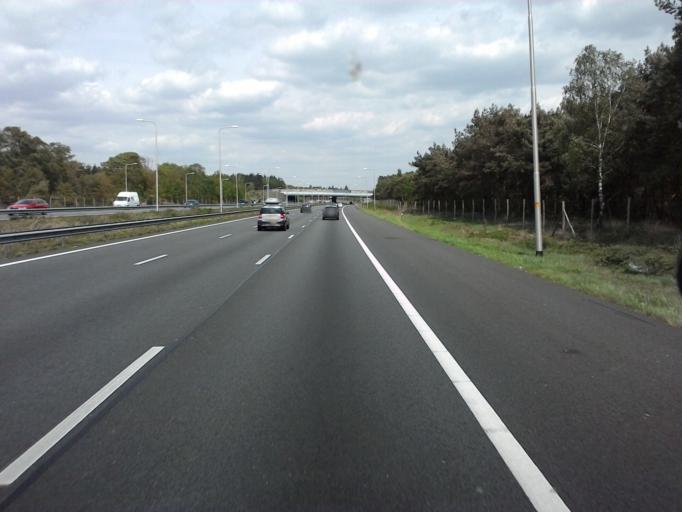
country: NL
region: Gelderland
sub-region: Gemeente Renkum
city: Wolfheze
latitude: 51.9928
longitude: 5.7820
